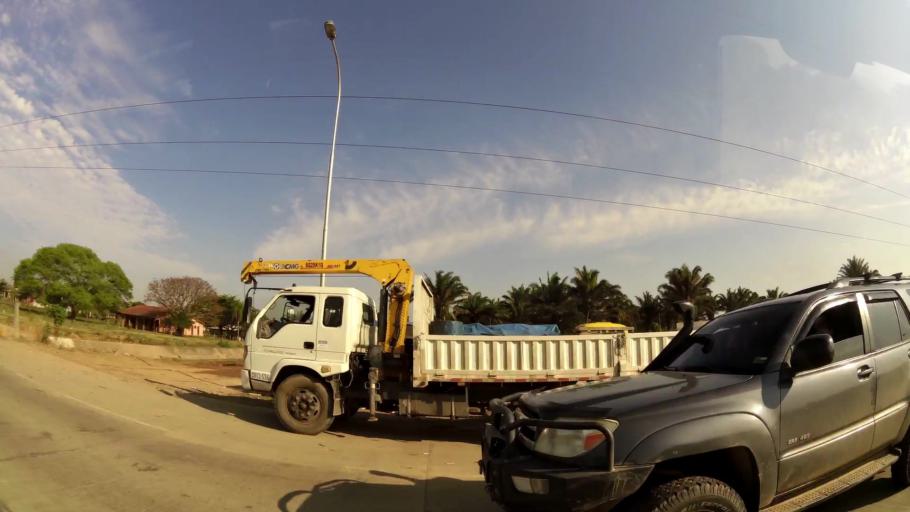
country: BO
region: Santa Cruz
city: Santa Cruz de la Sierra
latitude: -17.7199
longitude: -63.1308
